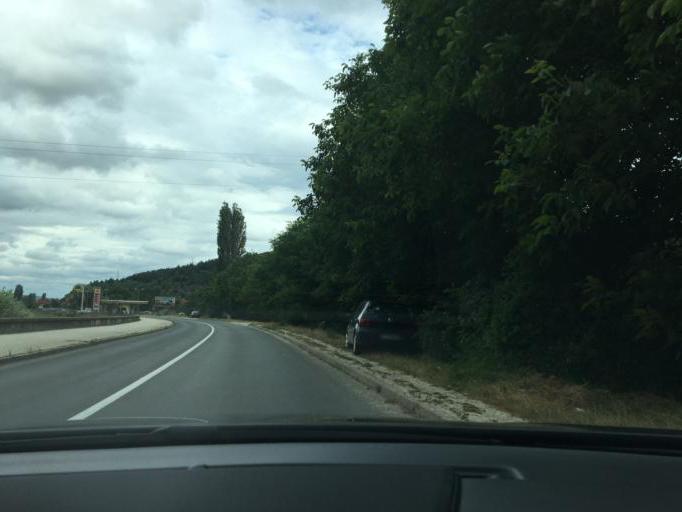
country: MK
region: Kriva Palanka
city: Kriva Palanka
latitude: 42.2006
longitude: 22.3281
